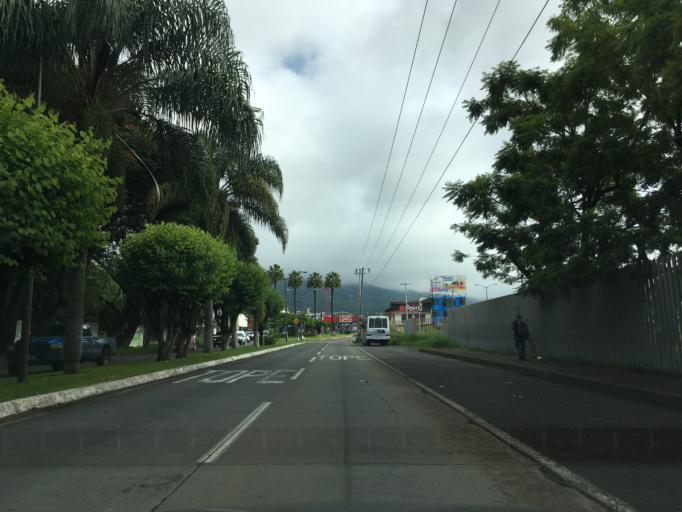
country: MX
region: Michoacan
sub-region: Uruapan
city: Uruapan
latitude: 19.4162
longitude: -102.0463
